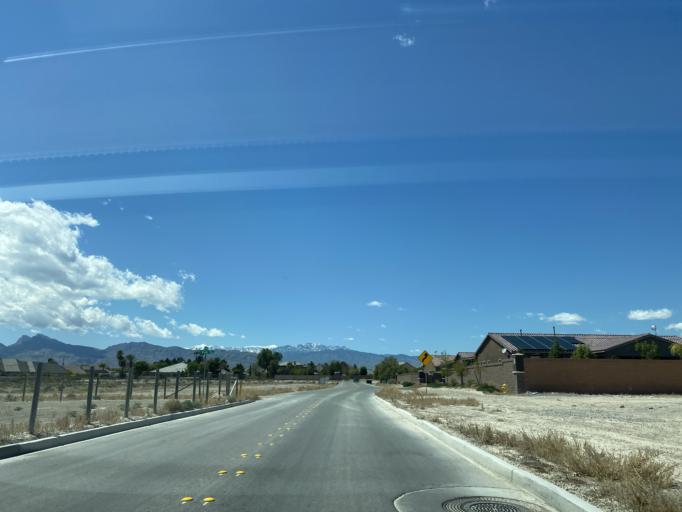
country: US
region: Nevada
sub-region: Clark County
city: North Las Vegas
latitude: 36.3109
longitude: -115.2350
